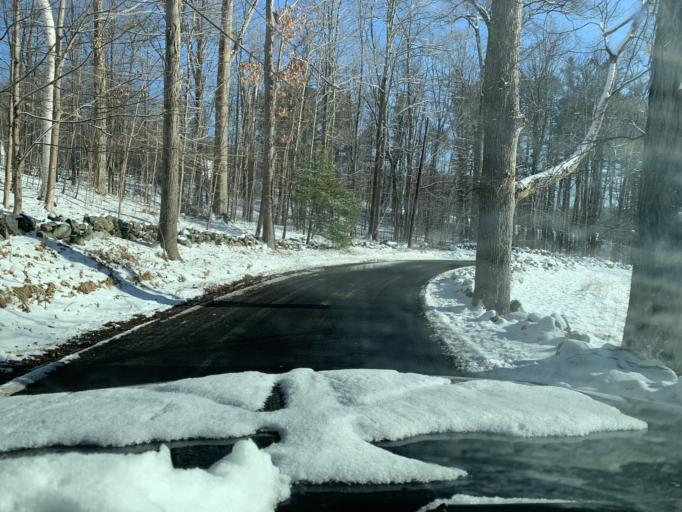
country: US
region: Massachusetts
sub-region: Essex County
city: Topsfield
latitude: 42.6332
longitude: -70.9592
